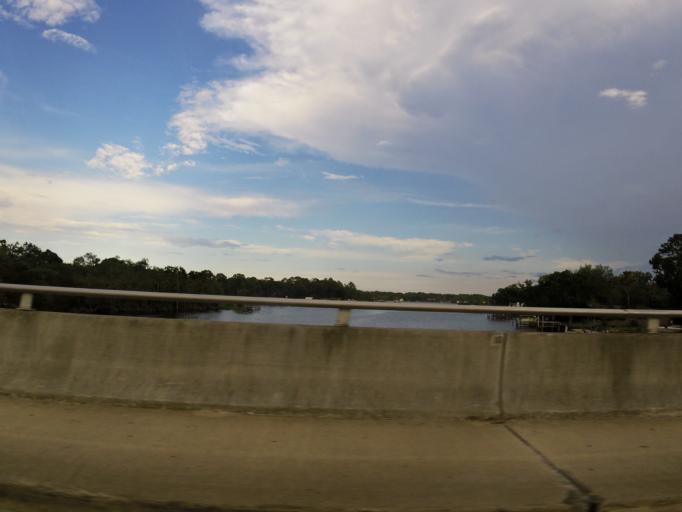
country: US
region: Florida
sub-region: Clay County
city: Bellair-Meadowbrook Terrace
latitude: 30.2729
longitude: -81.7334
